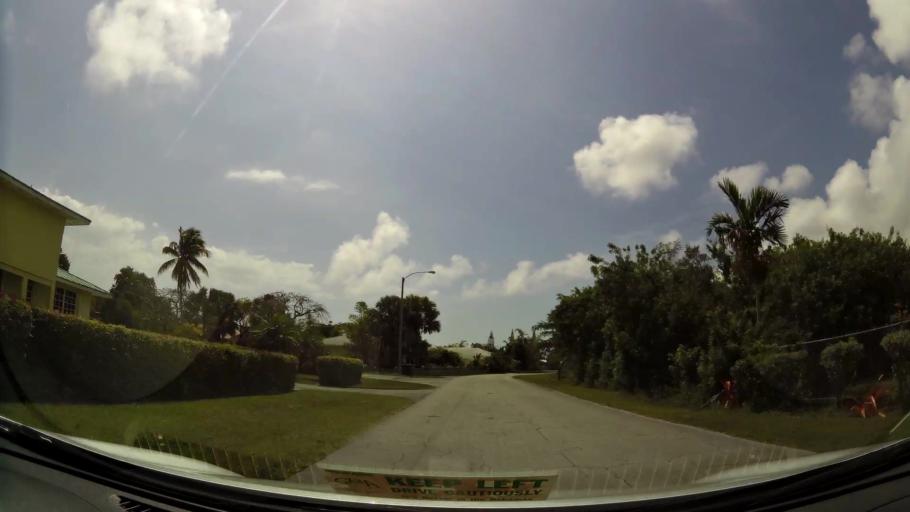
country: BS
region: Freeport
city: Freeport
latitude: 26.5094
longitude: -78.7076
